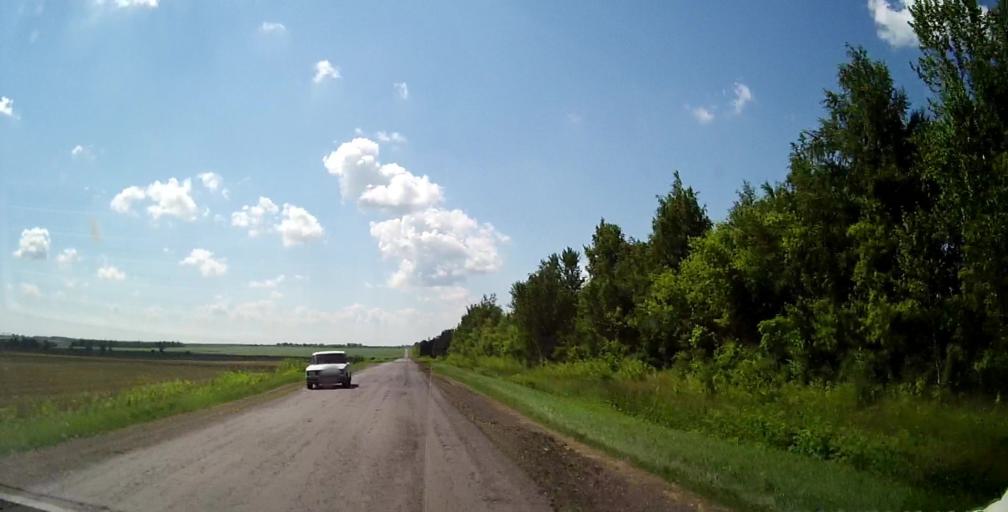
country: RU
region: Lipetsk
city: Chaplygin
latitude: 53.2895
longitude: 39.9584
